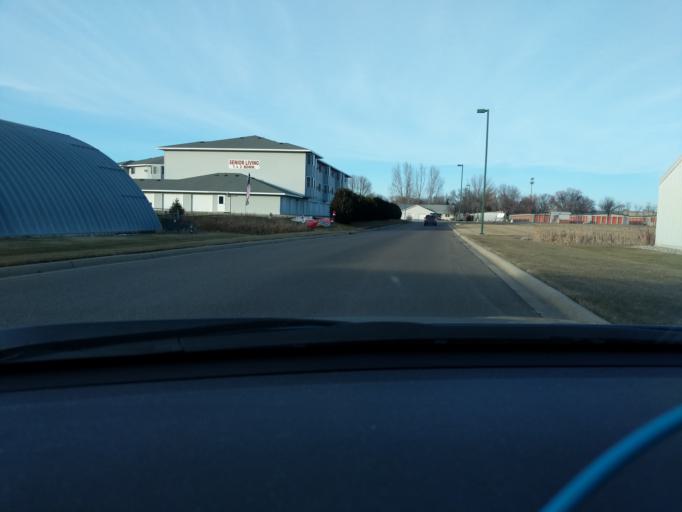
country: US
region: Minnesota
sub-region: Kandiyohi County
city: Willmar
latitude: 45.0948
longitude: -95.0450
